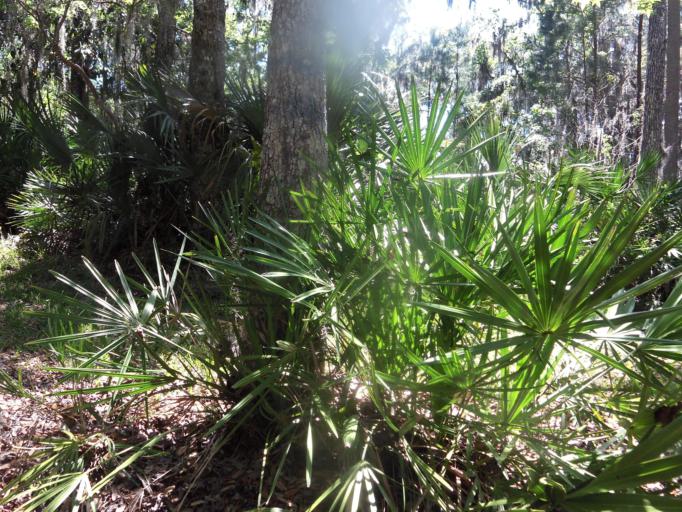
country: US
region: Florida
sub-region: Duval County
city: Atlantic Beach
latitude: 30.4432
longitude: -81.4787
